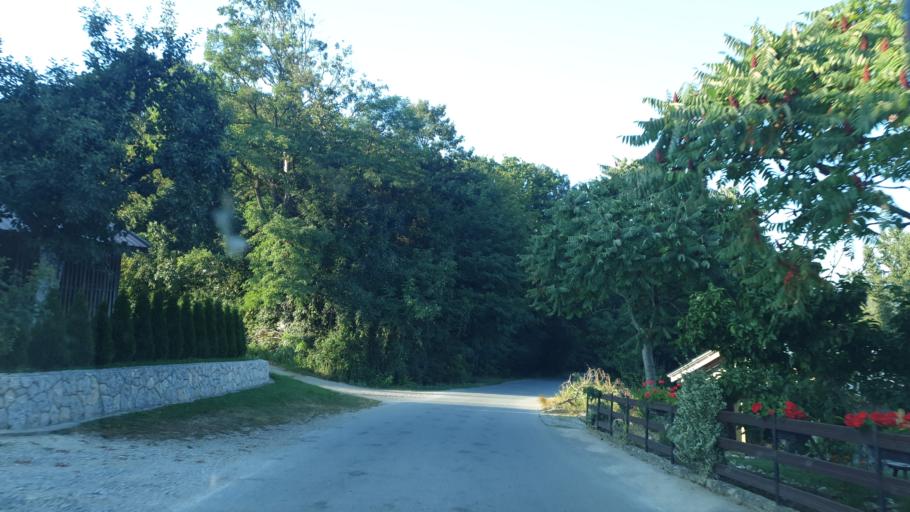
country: RS
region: Central Serbia
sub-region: Zlatiborski Okrug
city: Pozega
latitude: 43.8717
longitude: 19.9913
